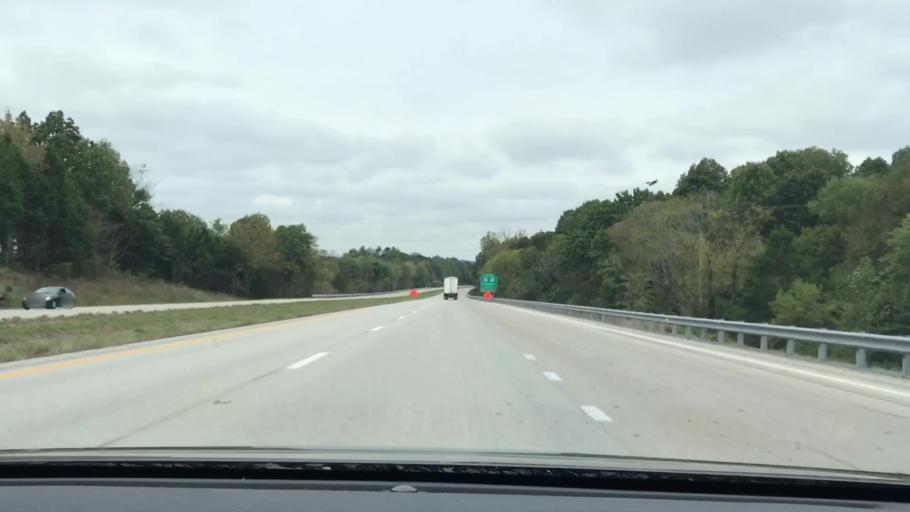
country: US
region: Kentucky
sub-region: Metcalfe County
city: Edmonton
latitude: 36.9993
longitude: -85.6224
